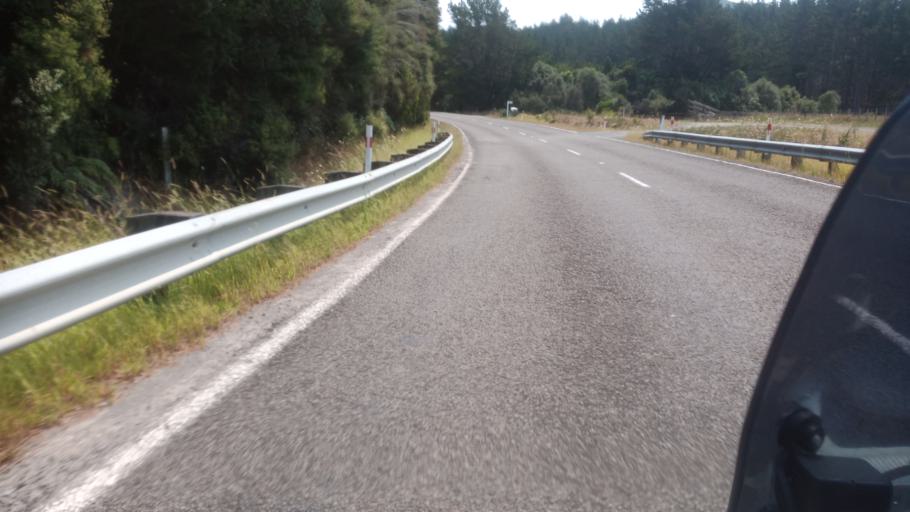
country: NZ
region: Bay of Plenty
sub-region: Opotiki District
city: Opotiki
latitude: -37.5765
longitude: 178.1148
